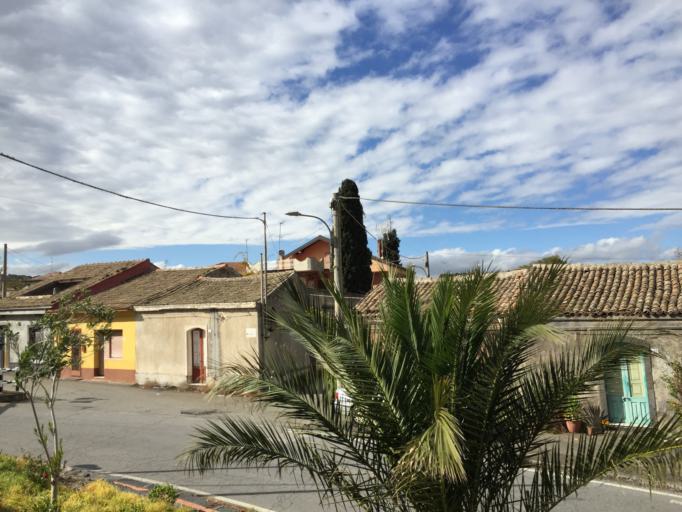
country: IT
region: Sicily
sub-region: Messina
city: Moio Alcantara
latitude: 37.8712
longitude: 15.0393
